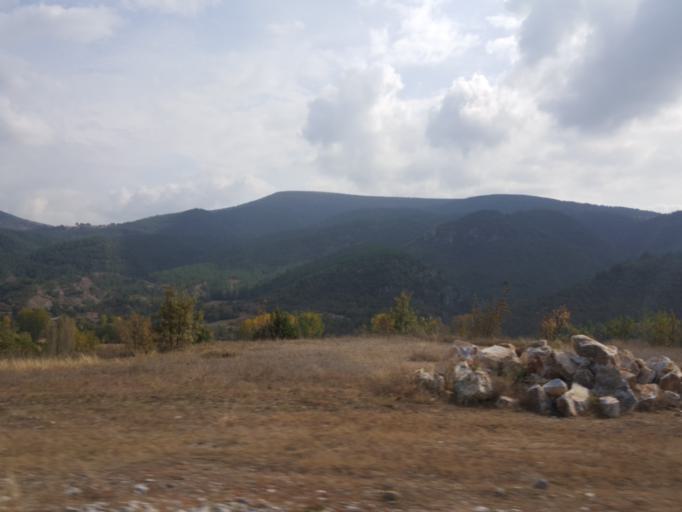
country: TR
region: Sinop
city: Sarayduzu
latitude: 41.3780
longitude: 34.9074
